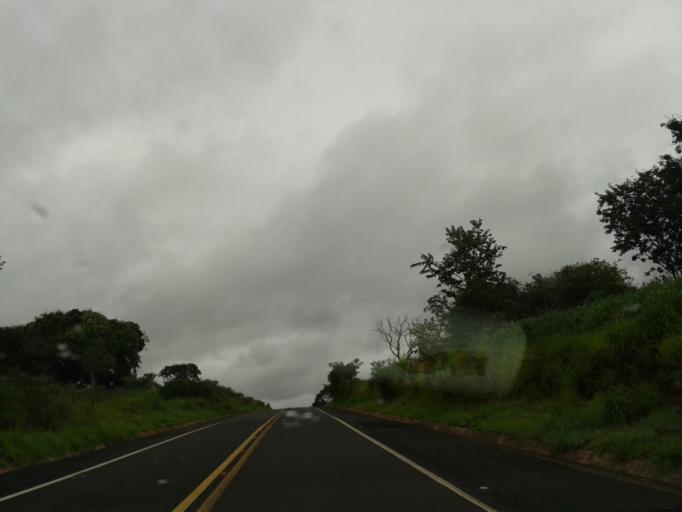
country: BR
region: Minas Gerais
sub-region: Santa Vitoria
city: Santa Vitoria
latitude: -19.2081
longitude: -50.0235
